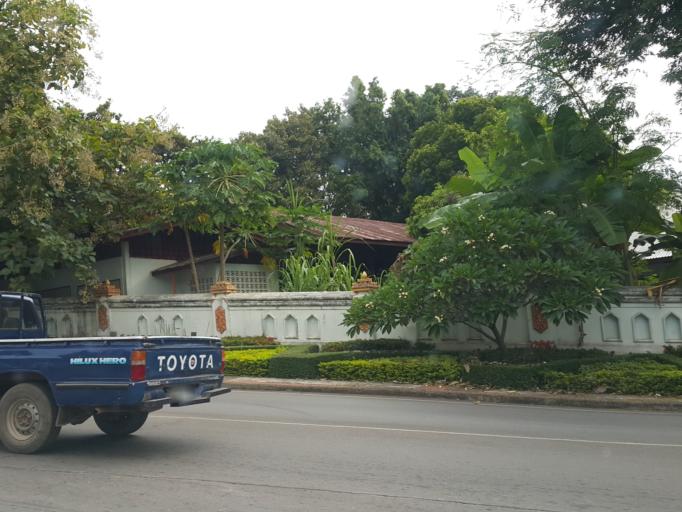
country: TH
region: Mae Hong Son
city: Mae Hong Son
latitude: 19.2970
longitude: 97.9634
